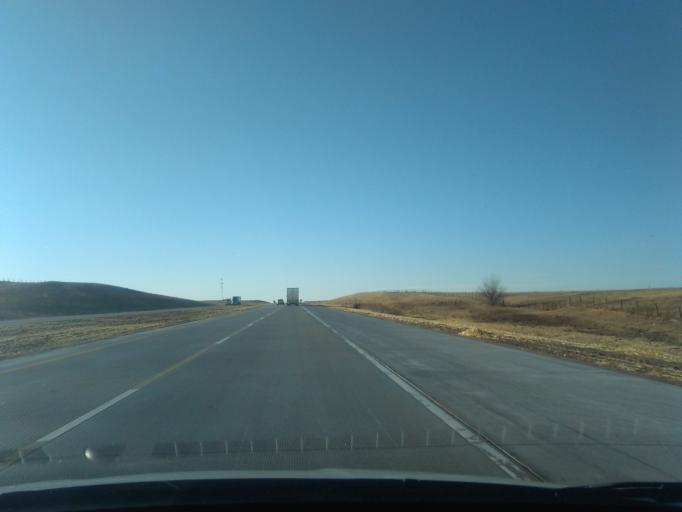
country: US
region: Nebraska
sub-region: Deuel County
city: Chappell
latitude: 41.1134
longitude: -102.5908
